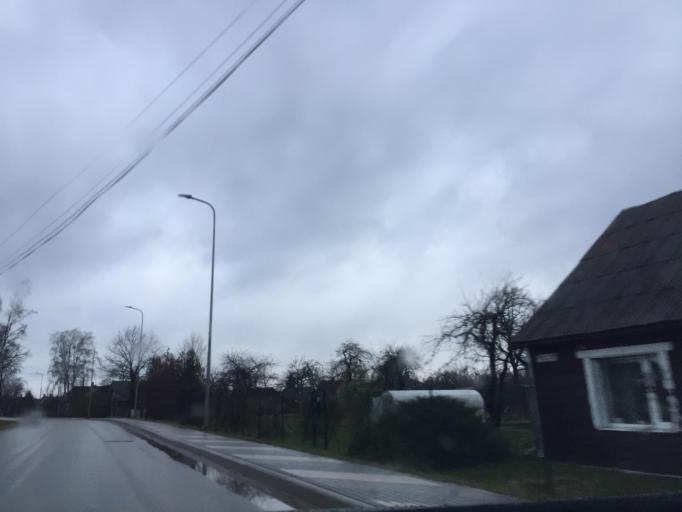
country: LV
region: Salacgrivas
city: Salacgriva
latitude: 57.7488
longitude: 24.3682
